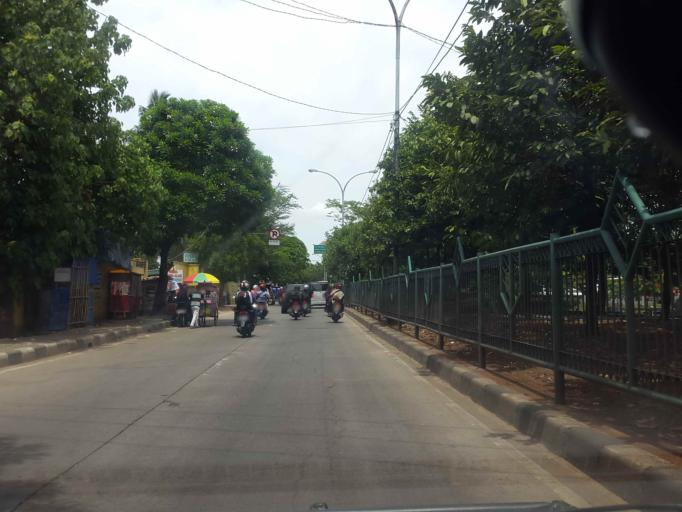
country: ID
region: Banten
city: Tangerang
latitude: -6.1515
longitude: 106.6325
